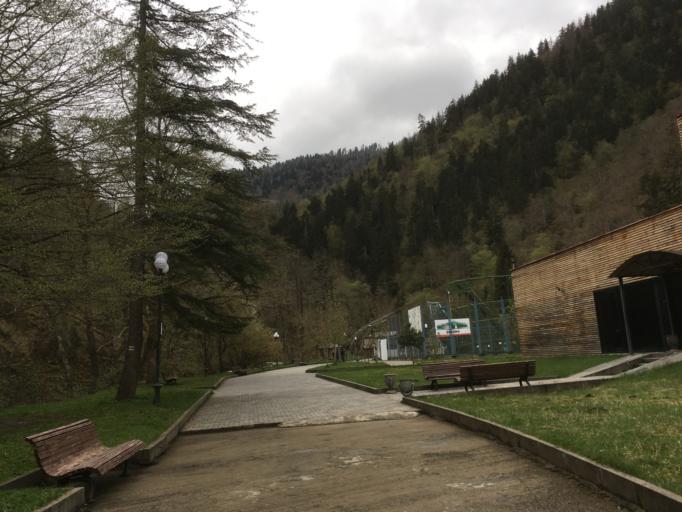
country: GE
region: Samtskhe-Javakheti
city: Borjomi
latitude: 41.8300
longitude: 43.3935
